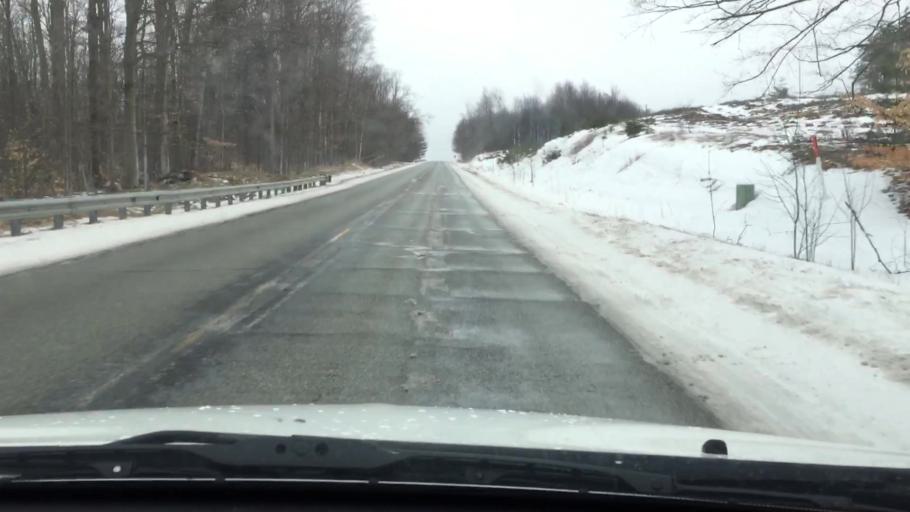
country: US
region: Michigan
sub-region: Wexford County
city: Cadillac
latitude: 44.1709
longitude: -85.4054
